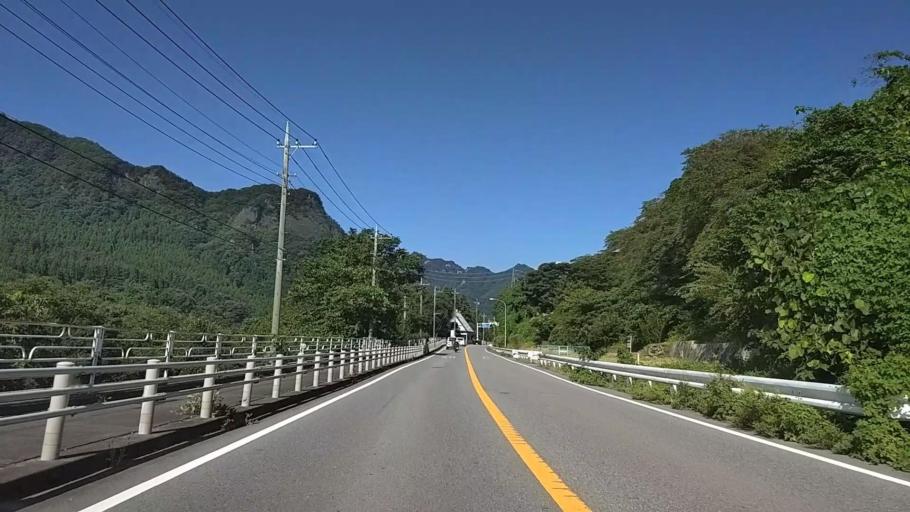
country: JP
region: Gunma
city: Annaka
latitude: 36.3338
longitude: 138.7457
